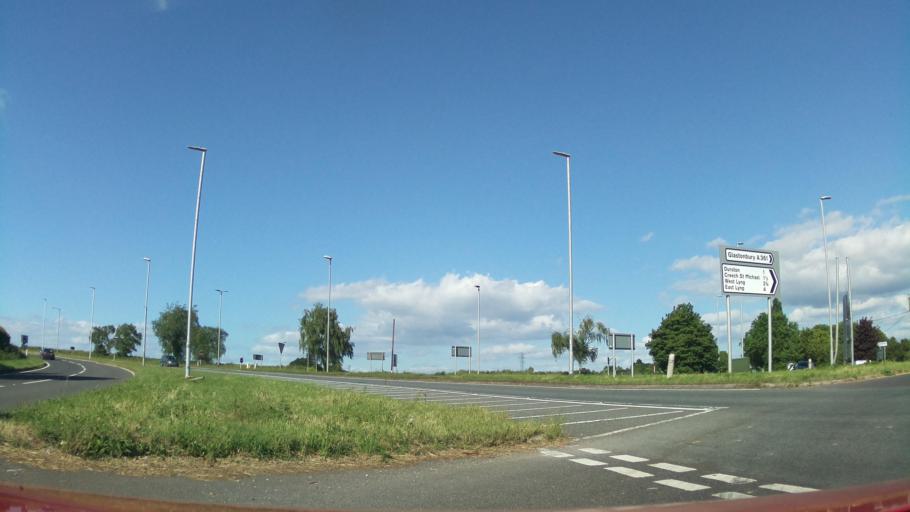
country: GB
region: England
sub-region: Somerset
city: Creech Saint Michael
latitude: 51.0471
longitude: -3.0331
